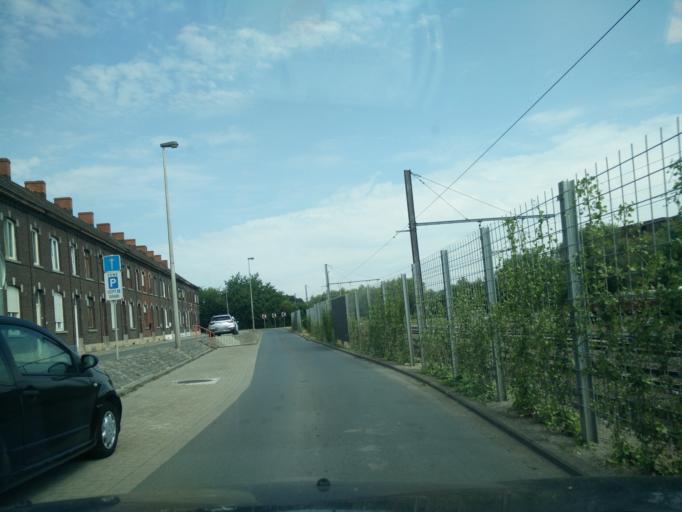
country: BE
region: Wallonia
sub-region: Province du Brabant Wallon
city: Tubize
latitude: 50.6917
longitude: 4.2146
